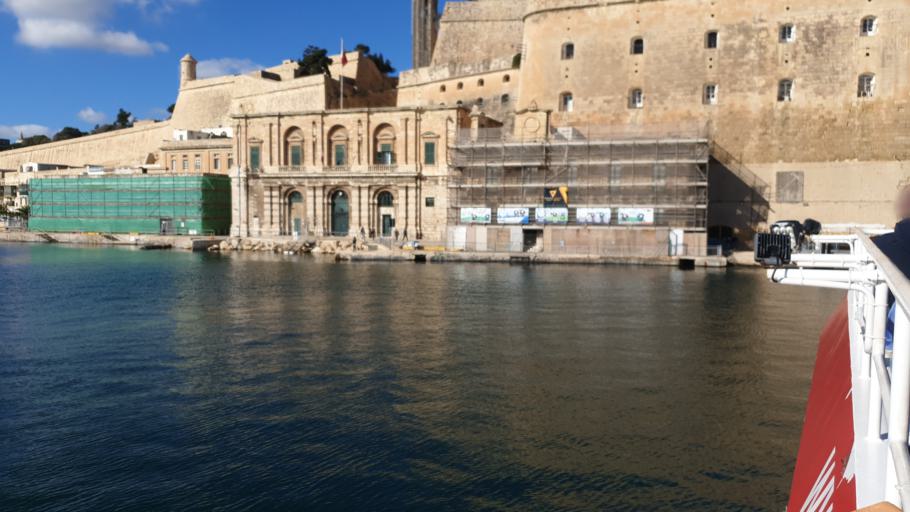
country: MT
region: Il-Birgu
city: Vittoriosa
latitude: 35.8938
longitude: 14.5139
